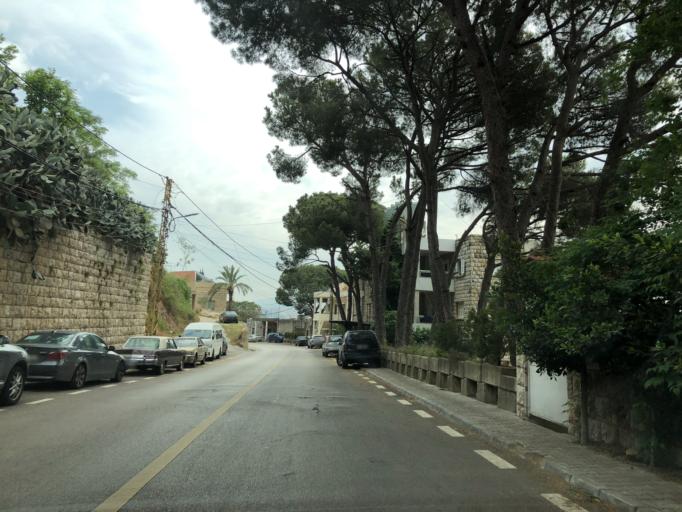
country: LB
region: Mont-Liban
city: Jdaidet el Matn
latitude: 33.8624
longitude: 35.6048
